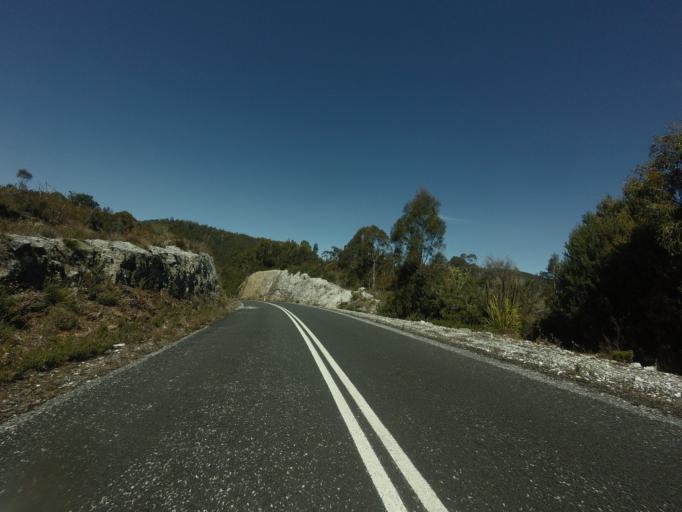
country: AU
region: Tasmania
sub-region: West Coast
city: Queenstown
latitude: -42.8008
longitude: 146.0924
